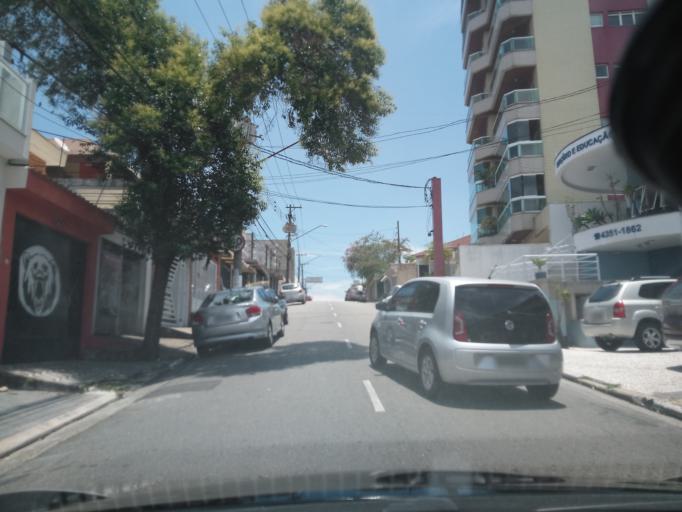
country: BR
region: Sao Paulo
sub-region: Sao Bernardo Do Campo
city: Sao Bernardo do Campo
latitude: -23.7205
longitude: -46.5684
